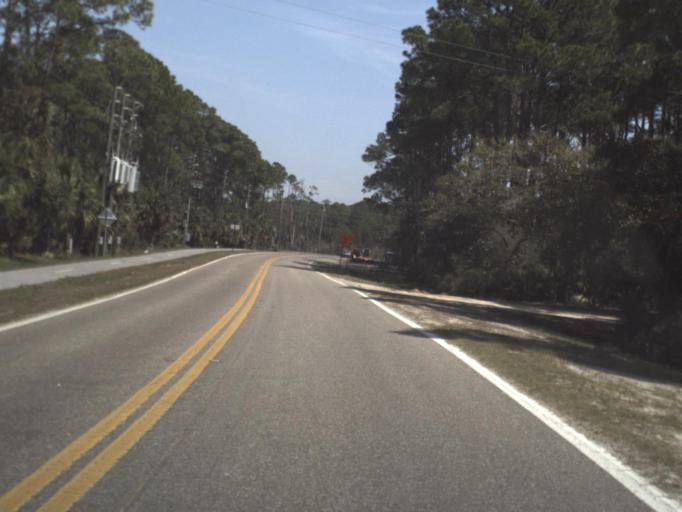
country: US
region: Florida
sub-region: Gulf County
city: Port Saint Joe
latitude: 29.6853
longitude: -85.3111
